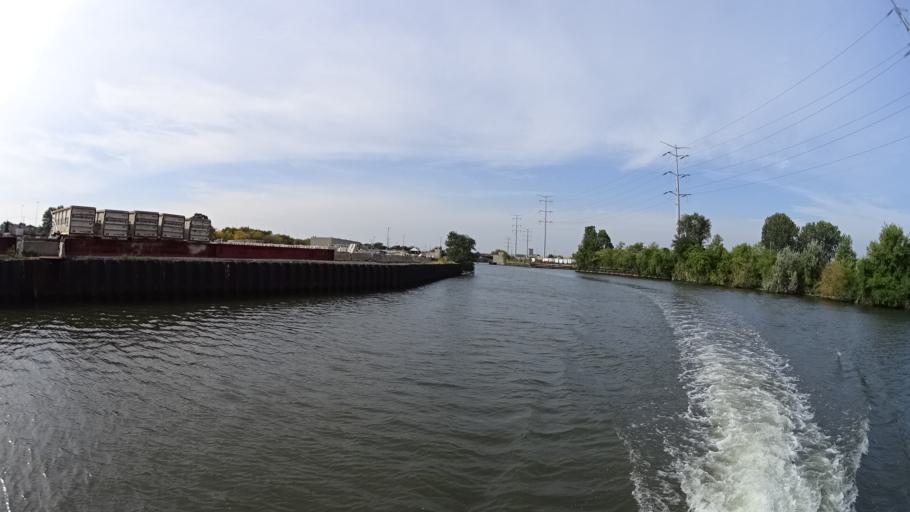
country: US
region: Illinois
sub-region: Cook County
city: Chicago
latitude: 41.8482
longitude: -87.6566
